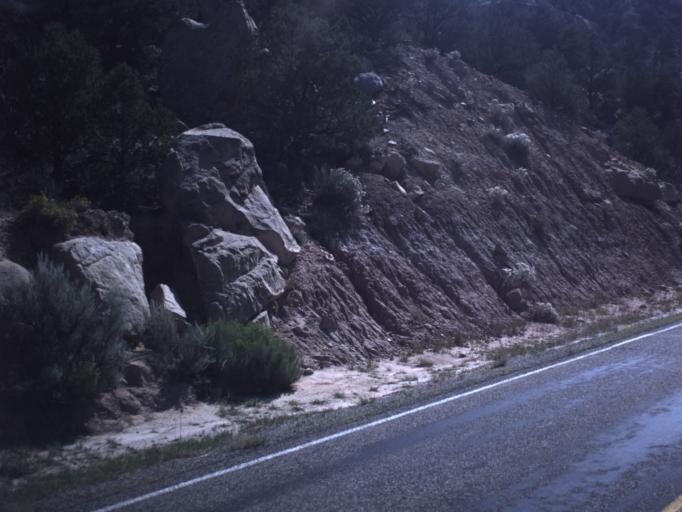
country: US
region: Utah
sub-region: Duchesne County
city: Duchesne
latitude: 40.3136
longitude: -110.6419
